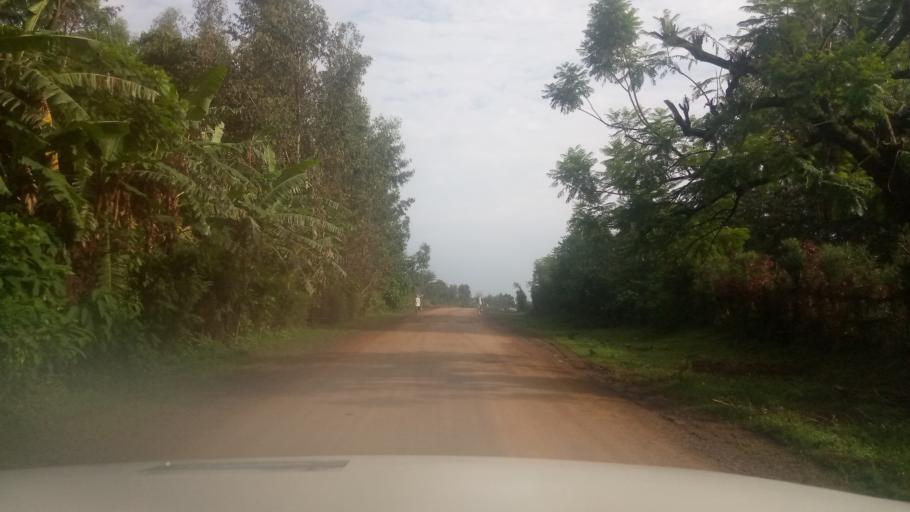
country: ET
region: Oromiya
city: Agaro
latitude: 7.8494
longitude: 36.6560
